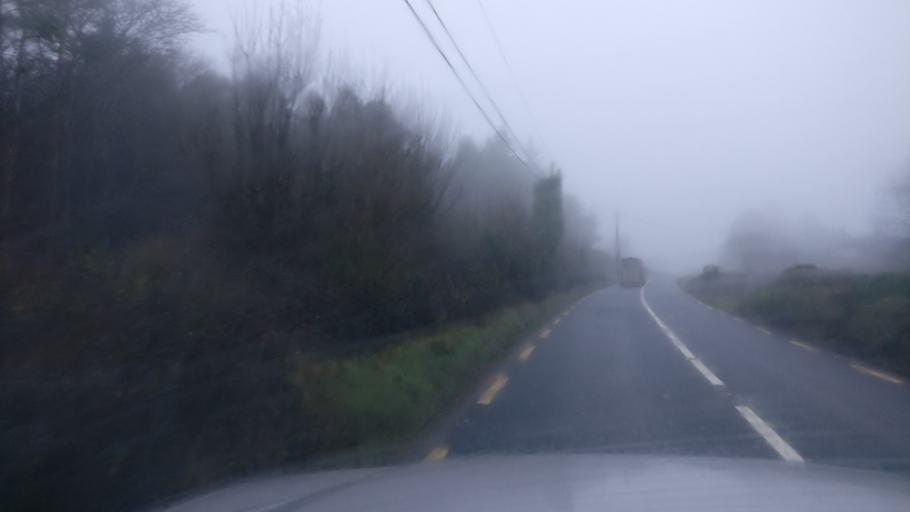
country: IE
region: Connaught
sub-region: County Galway
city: Loughrea
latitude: 53.1699
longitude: -8.6690
